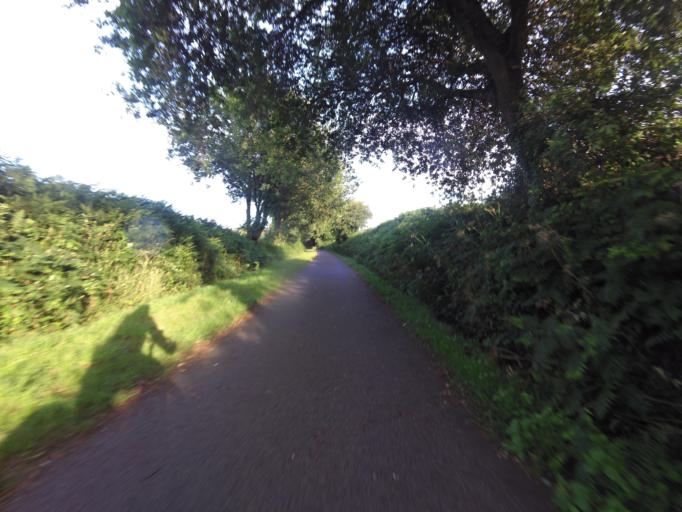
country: FR
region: Brittany
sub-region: Departement du Morbihan
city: Malestroit
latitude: 47.8187
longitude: -2.4167
